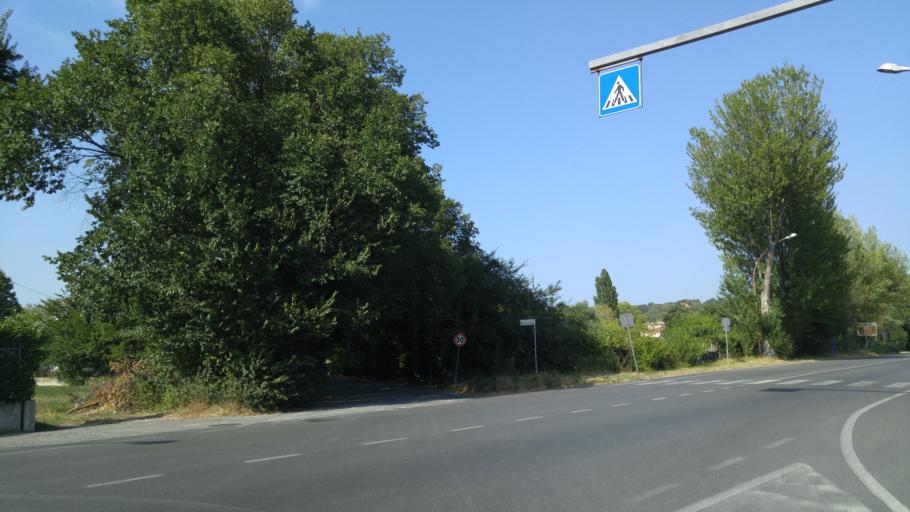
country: IT
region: The Marches
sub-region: Provincia di Pesaro e Urbino
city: Pesaro
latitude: 43.8960
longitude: 12.9146
